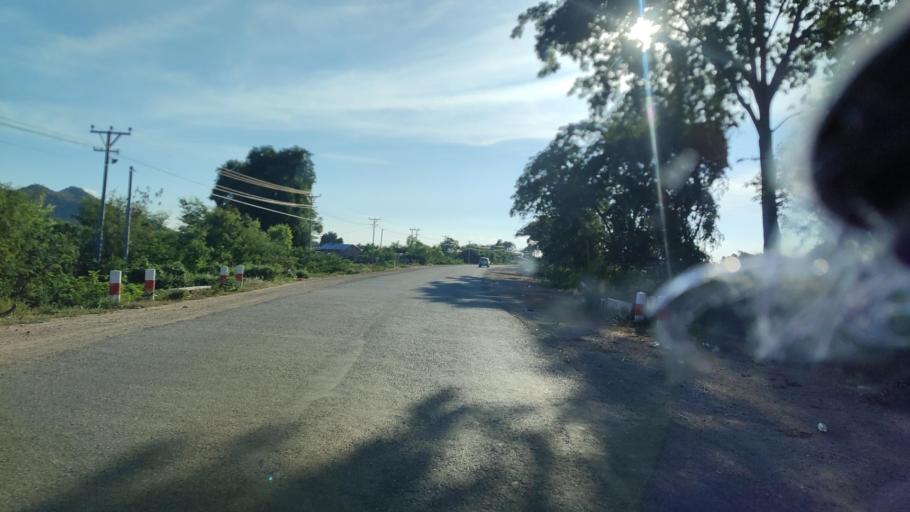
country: MM
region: Mandalay
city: Yamethin
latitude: 20.7381
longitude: 96.2100
